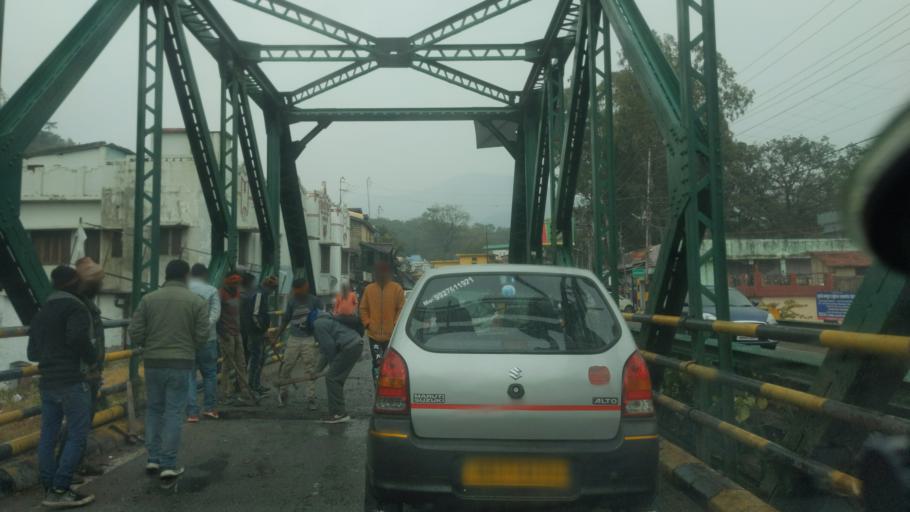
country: IN
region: Uttarakhand
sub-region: Naini Tal
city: Haldwani
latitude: 29.2706
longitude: 79.5440
